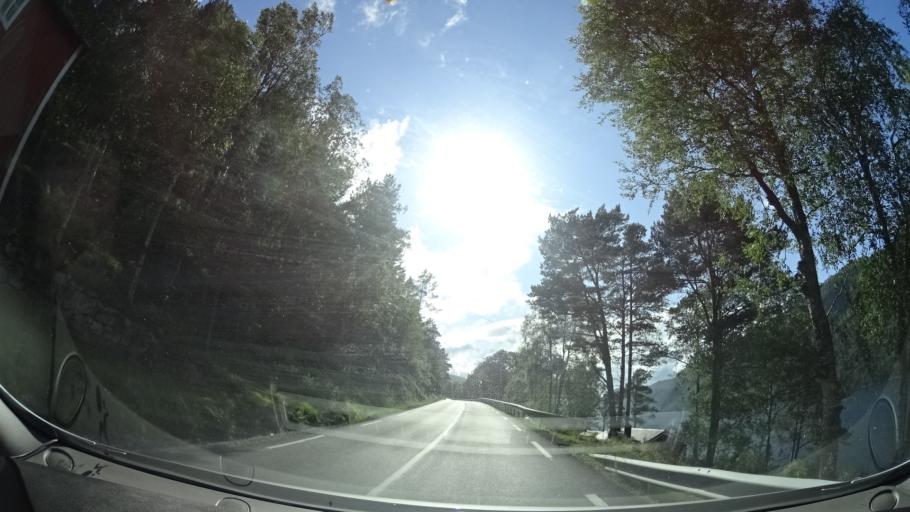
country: NO
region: Sor-Trondelag
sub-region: Hemne
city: Kyrksaeterora
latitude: 63.2006
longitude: 8.9698
